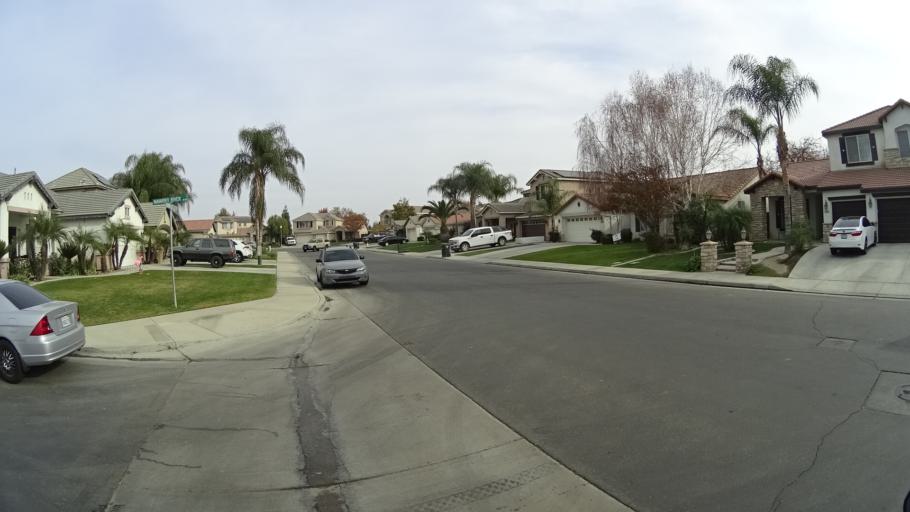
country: US
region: California
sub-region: Kern County
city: Rosedale
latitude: 35.3406
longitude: -119.1416
